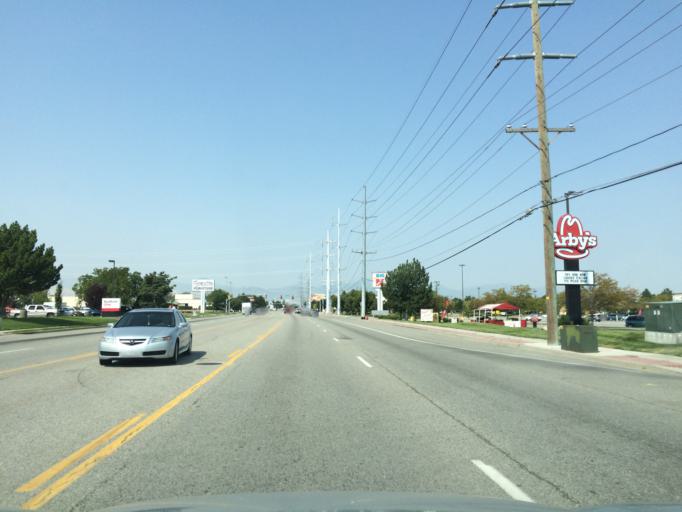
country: US
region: Utah
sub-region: Salt Lake County
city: West Jordan
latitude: 40.5879
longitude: -111.9314
